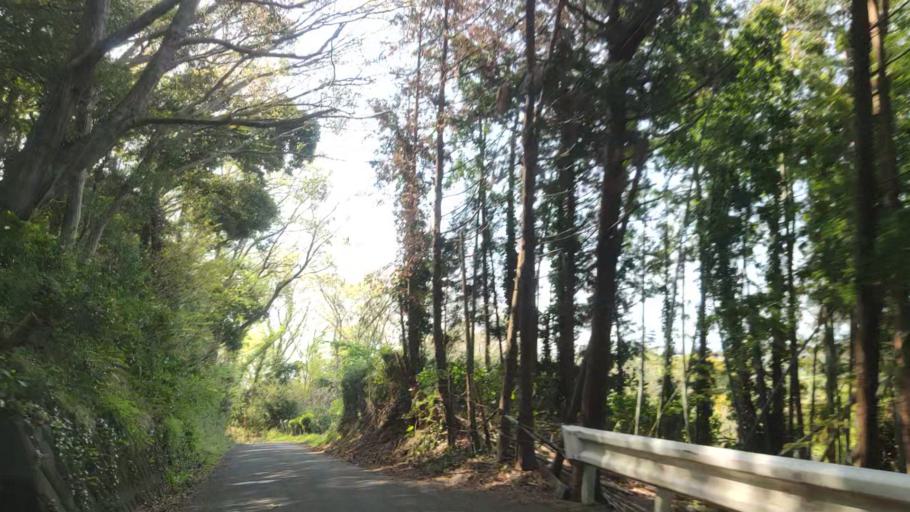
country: JP
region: Kanagawa
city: Ninomiya
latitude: 35.3259
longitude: 139.2674
